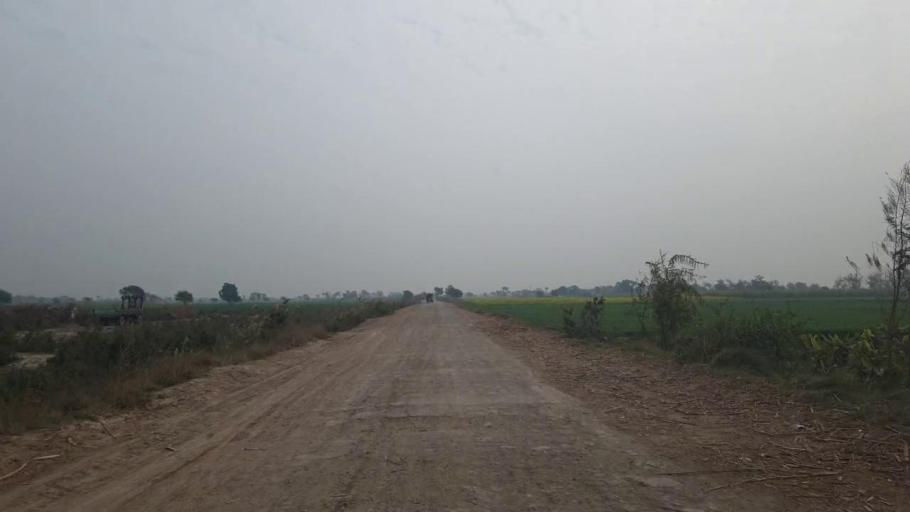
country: PK
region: Sindh
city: Tando Adam
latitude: 25.7243
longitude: 68.7291
